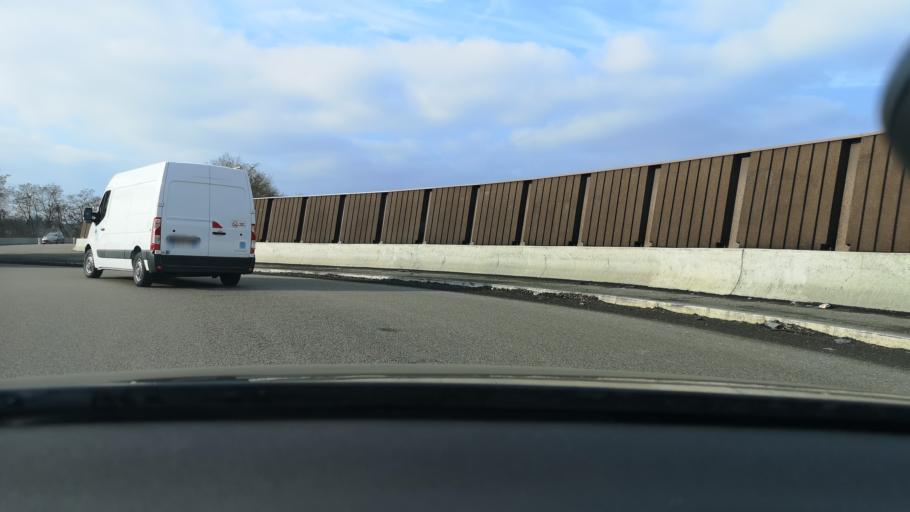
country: FR
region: Bourgogne
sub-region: Departement de Saone-et-Loire
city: Saint-Remy
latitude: 46.7577
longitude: 4.8337
